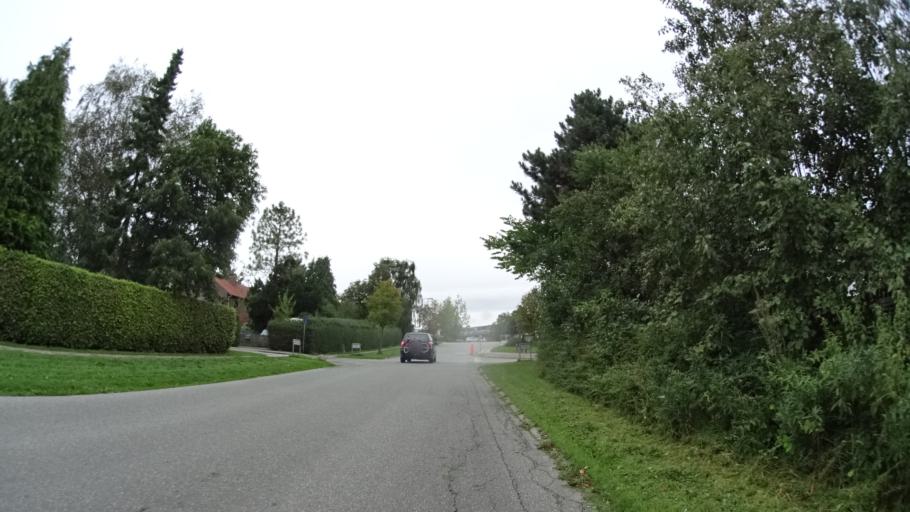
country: DK
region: Central Jutland
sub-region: Arhus Kommune
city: Arhus
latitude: 56.1653
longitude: 10.1606
